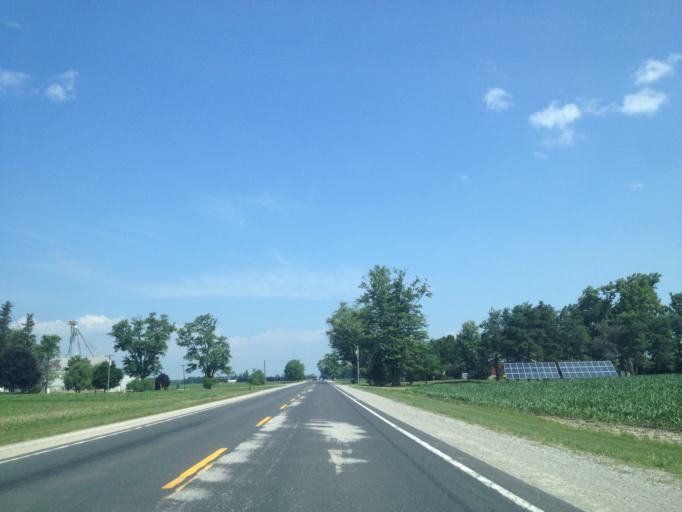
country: CA
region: Ontario
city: Stratford
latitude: 43.3248
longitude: -81.2038
